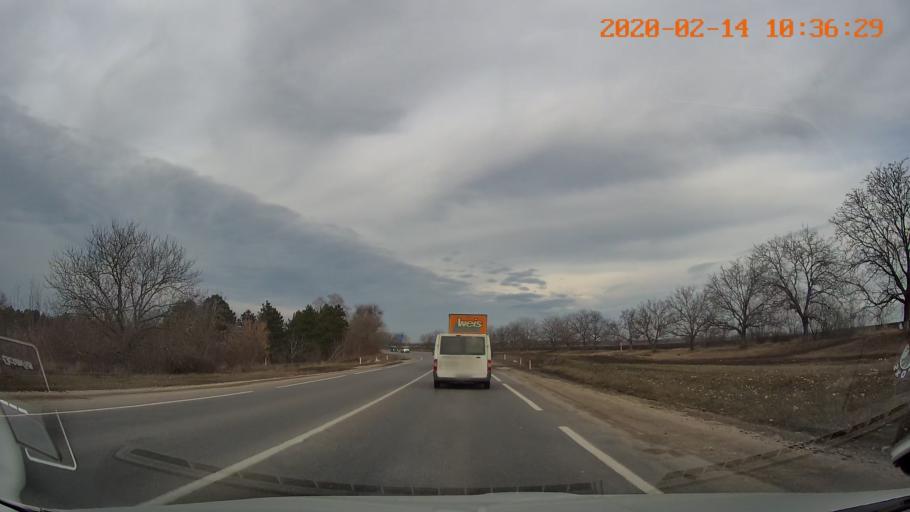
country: MD
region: Riscani
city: Riscani
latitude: 47.9259
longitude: 27.6445
